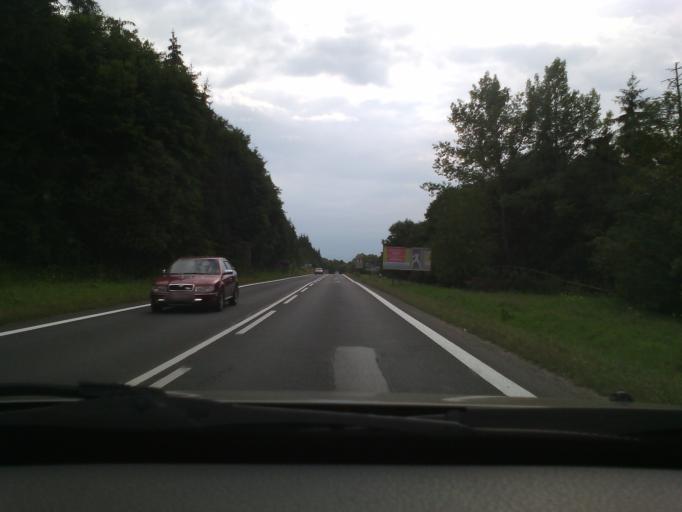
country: SK
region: Presovsky
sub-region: Okres Presov
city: Kezmarok
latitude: 49.1292
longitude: 20.4167
